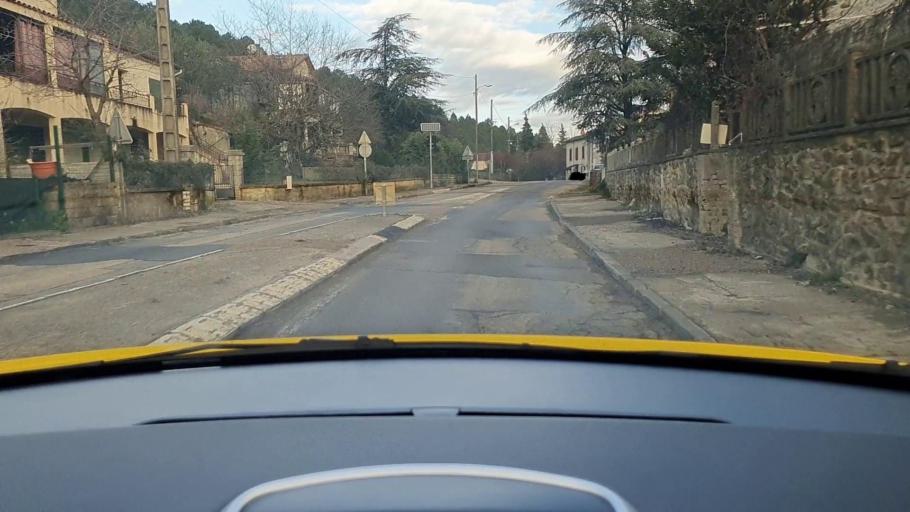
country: FR
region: Languedoc-Roussillon
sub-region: Departement du Gard
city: Laval-Pradel
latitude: 44.2338
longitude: 4.0563
